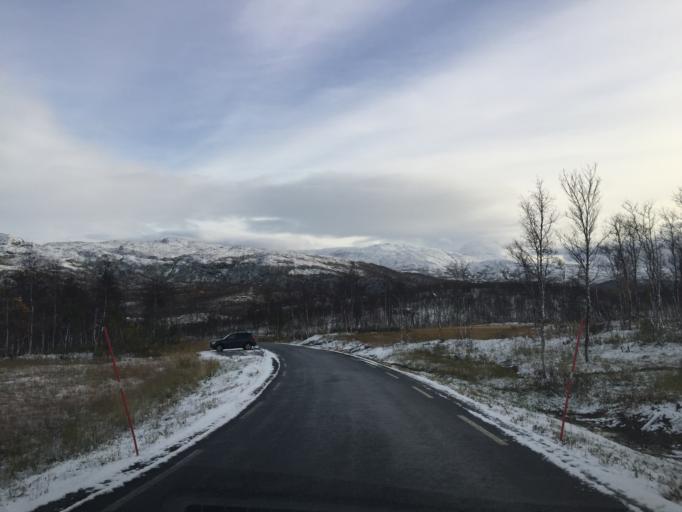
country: NO
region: Nordland
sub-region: Sorfold
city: Straumen
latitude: 67.0858
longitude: 16.0236
